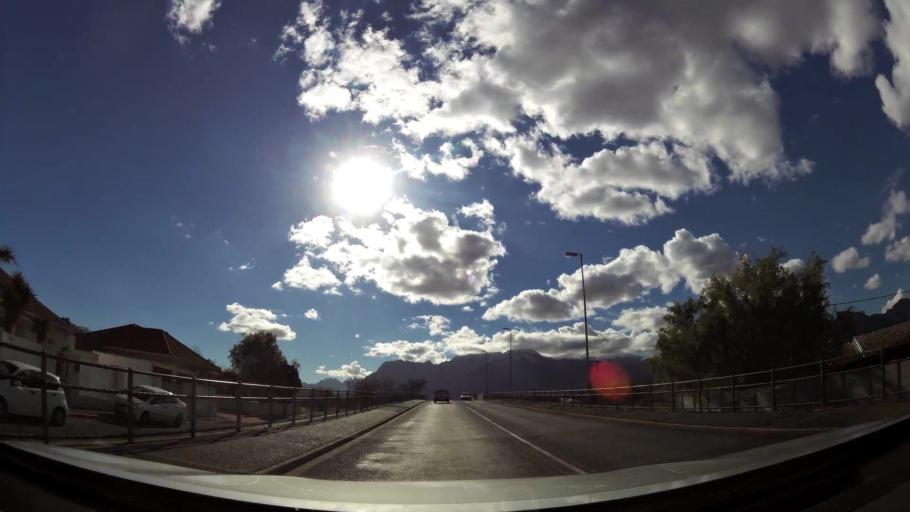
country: ZA
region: Western Cape
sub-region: Cape Winelands District Municipality
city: Worcester
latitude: -33.6410
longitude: 19.4321
